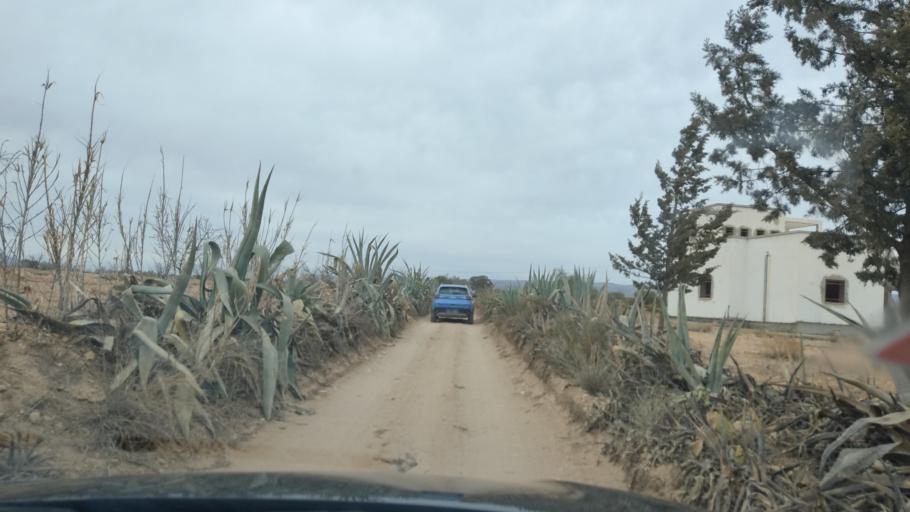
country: TN
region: Al Qasrayn
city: Kasserine
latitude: 35.2265
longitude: 8.9330
